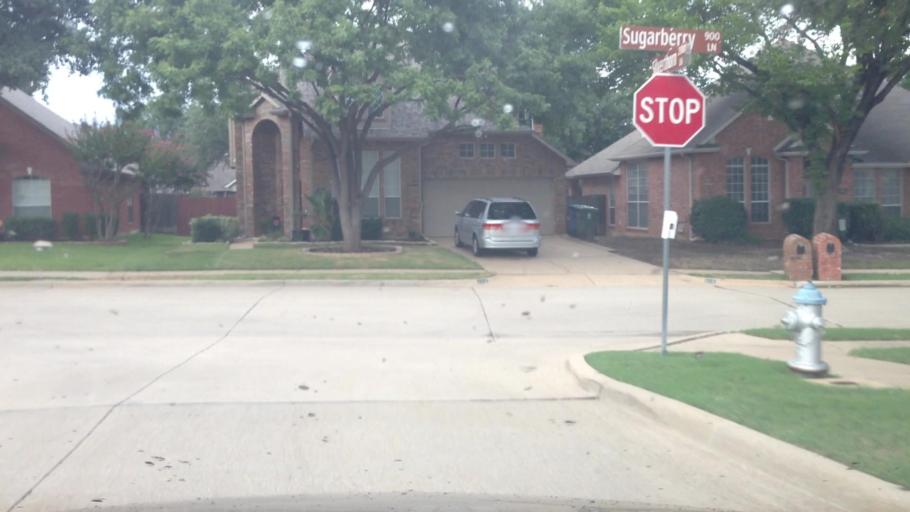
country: US
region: Texas
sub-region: Denton County
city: Flower Mound
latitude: 33.0172
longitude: -97.0433
